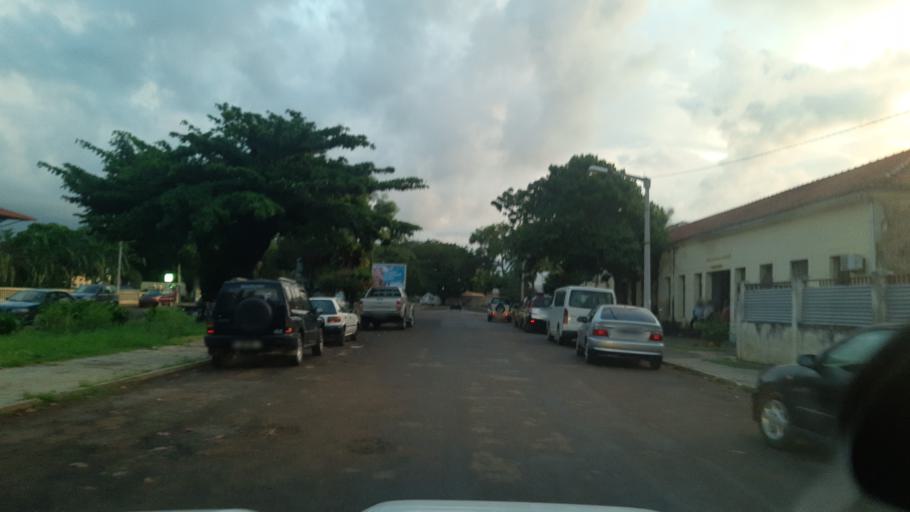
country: ST
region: Sao Tome Island
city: Sao Tome
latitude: 0.3453
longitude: 6.7384
